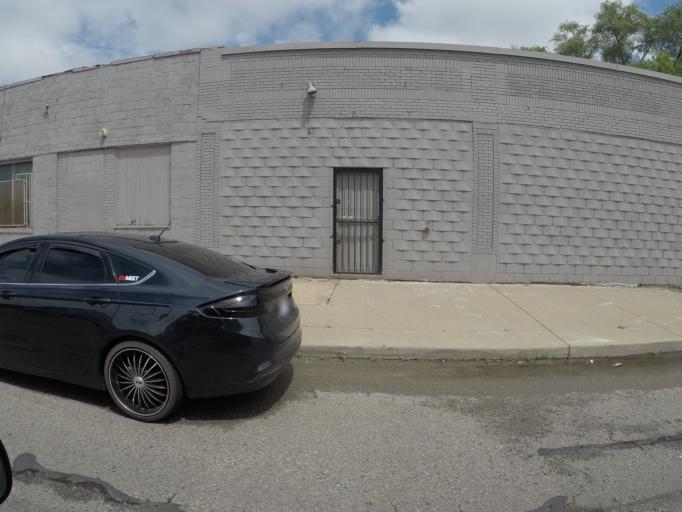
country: US
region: Michigan
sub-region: Wayne County
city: Dearborn
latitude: 42.3451
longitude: -83.1366
